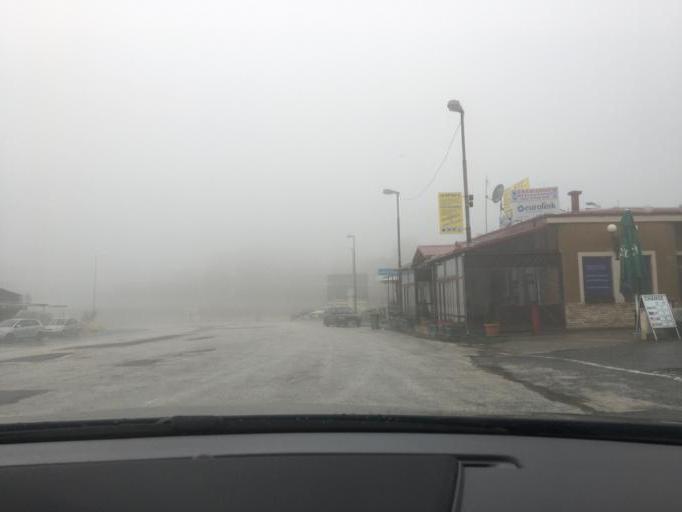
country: MK
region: Kriva Palanka
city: Kriva Palanka
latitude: 42.2210
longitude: 22.4587
